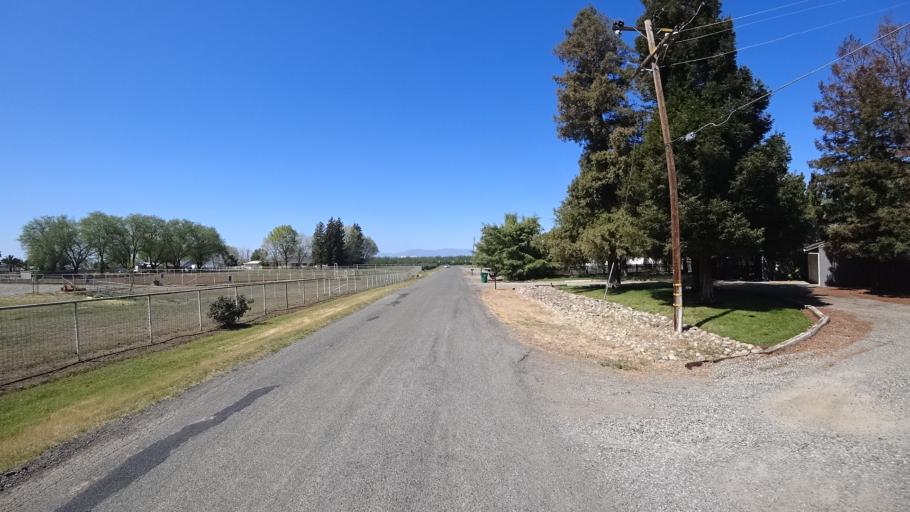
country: US
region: California
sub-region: Glenn County
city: Willows
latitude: 39.5334
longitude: -122.2098
